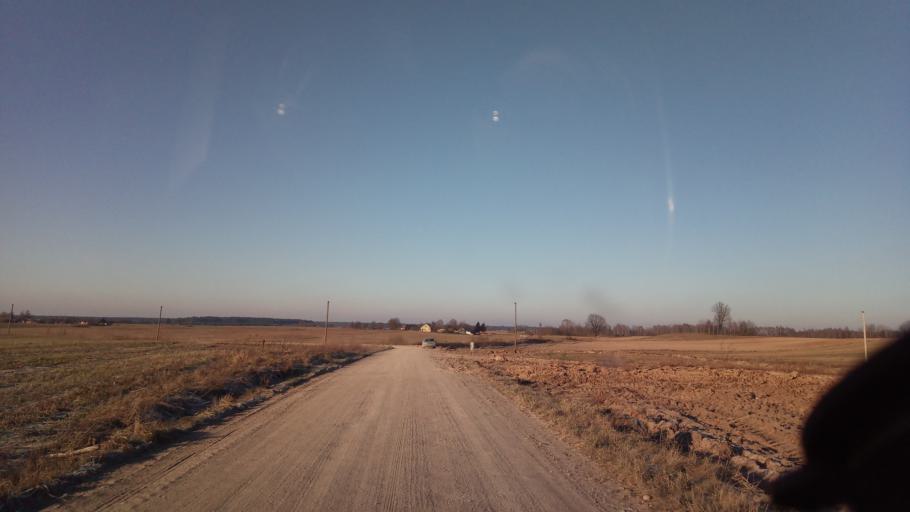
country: LT
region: Alytaus apskritis
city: Druskininkai
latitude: 54.0912
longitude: 23.9952
